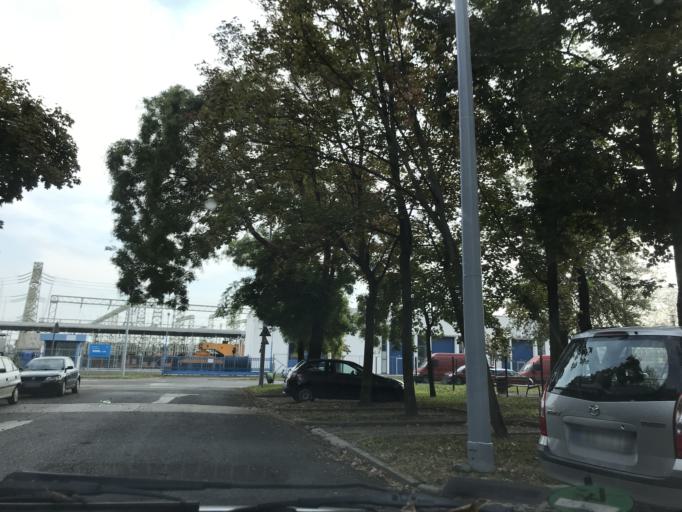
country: HU
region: Budapest
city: Budapest XIV. keruelet
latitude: 47.5335
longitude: 19.1314
